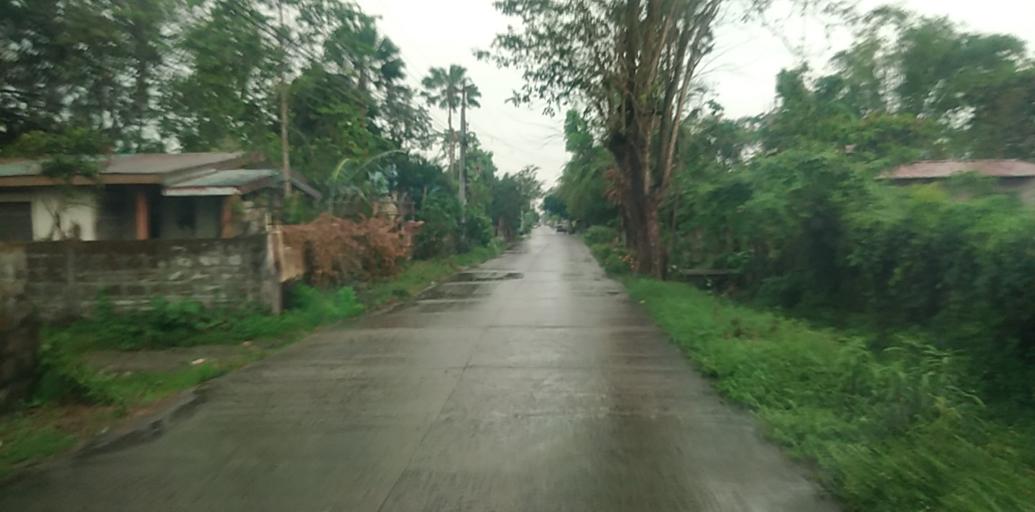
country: PH
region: Central Luzon
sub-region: Province of Pampanga
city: Arenas
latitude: 15.1659
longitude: 120.6888
